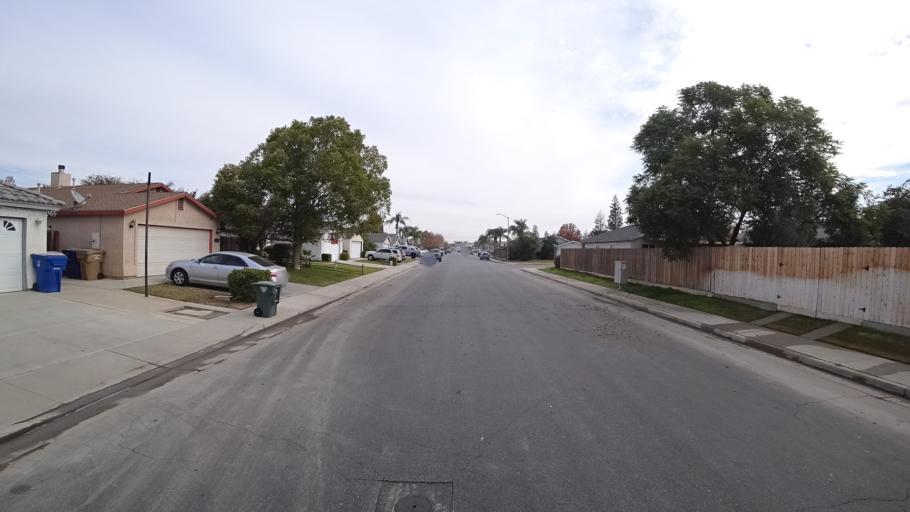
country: US
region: California
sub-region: Kern County
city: Rosedale
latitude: 35.4001
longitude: -119.1310
